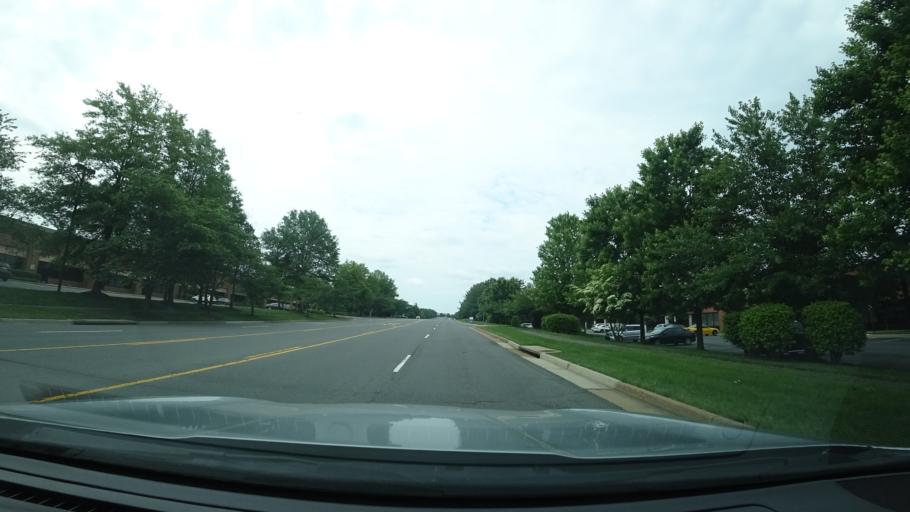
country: US
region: Virginia
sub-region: Loudoun County
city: Dulles Town Center
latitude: 39.0293
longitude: -77.4128
